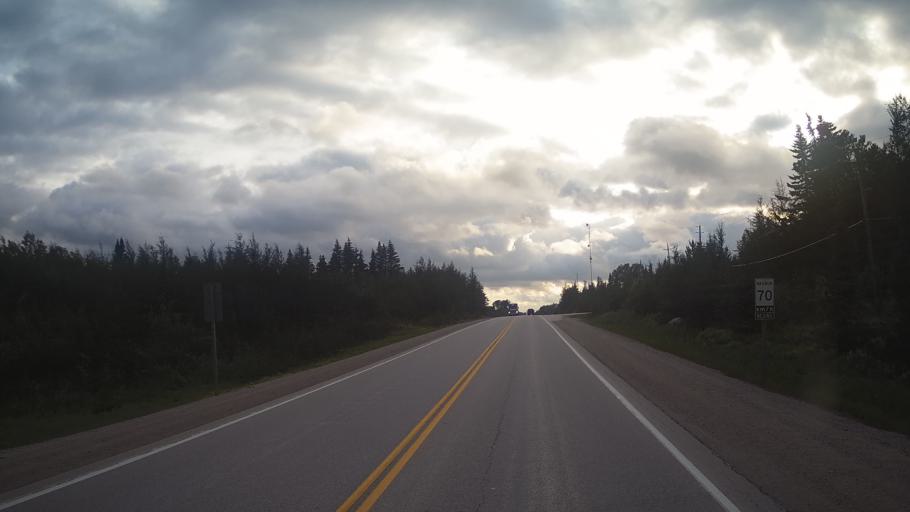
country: CA
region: Ontario
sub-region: Rainy River District
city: Atikokan
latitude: 49.0509
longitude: -90.4783
